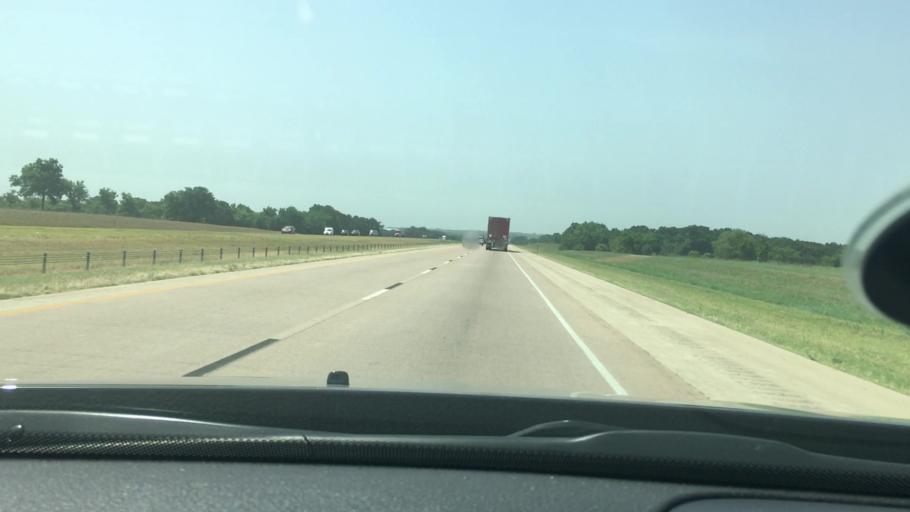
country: US
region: Oklahoma
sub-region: Garvin County
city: Pauls Valley
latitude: 34.6787
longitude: -97.2274
